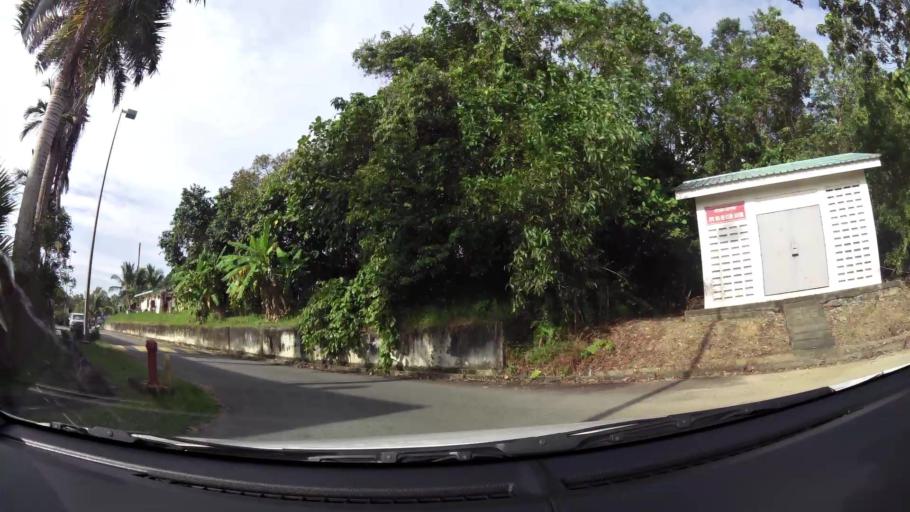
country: BN
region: Brunei and Muara
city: Bandar Seri Begawan
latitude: 4.9091
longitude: 114.8924
